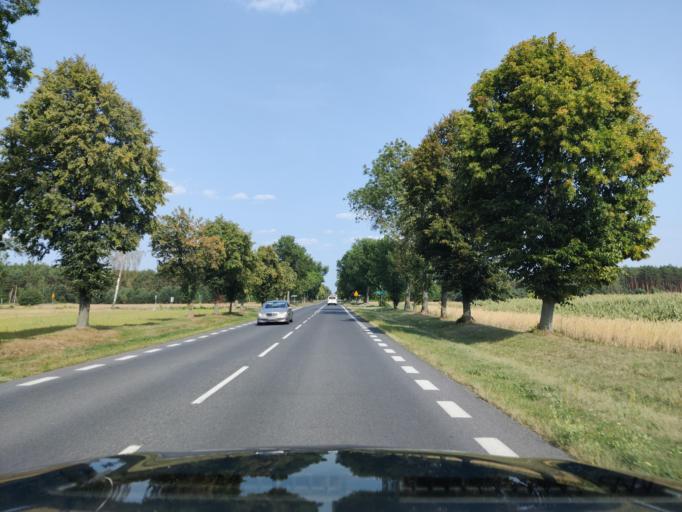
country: PL
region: Masovian Voivodeship
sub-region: Powiat makowski
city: Szelkow
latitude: 52.8333
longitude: 21.2393
